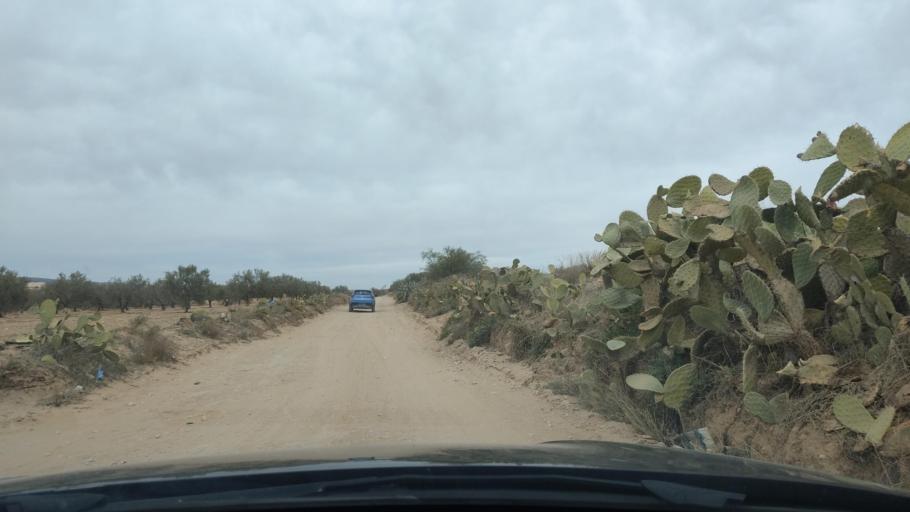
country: TN
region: Al Qasrayn
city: Kasserine
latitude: 35.2475
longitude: 8.9198
